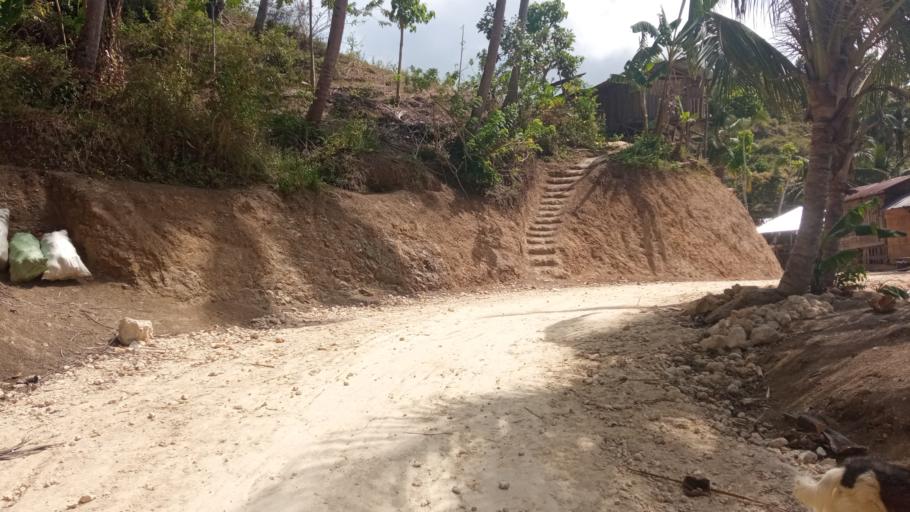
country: PH
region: Central Visayas
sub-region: Province of Siquijor
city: Lazi
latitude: 9.1558
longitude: 123.5787
